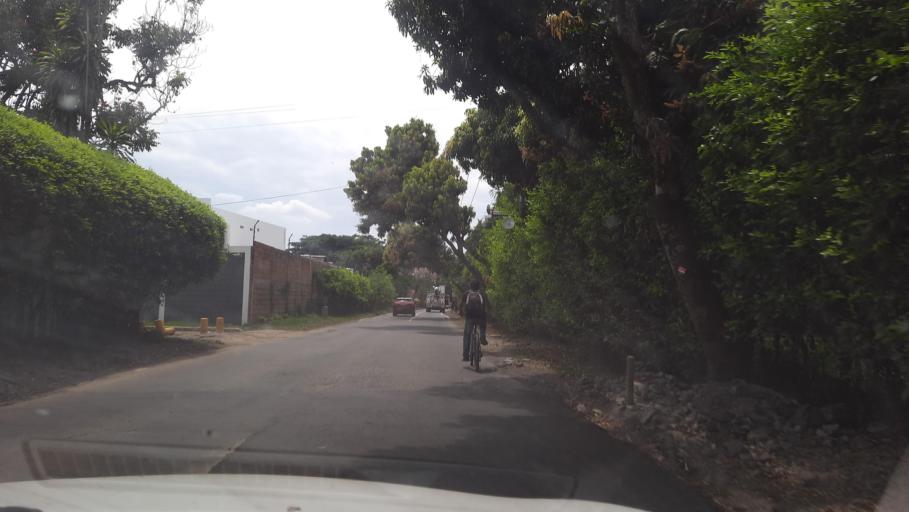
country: CO
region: Valle del Cauca
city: Jamundi
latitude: 3.2705
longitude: -76.5263
